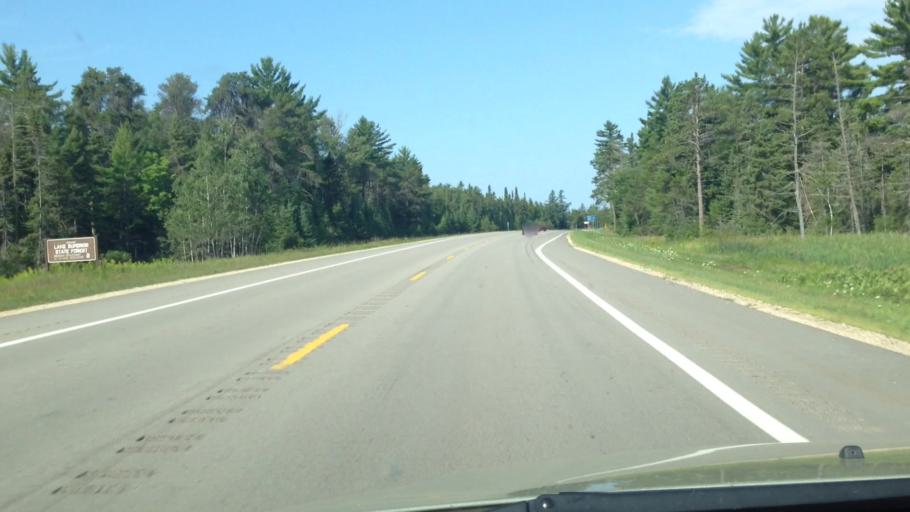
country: US
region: Michigan
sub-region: Schoolcraft County
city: Manistique
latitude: 45.8910
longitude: -86.5184
